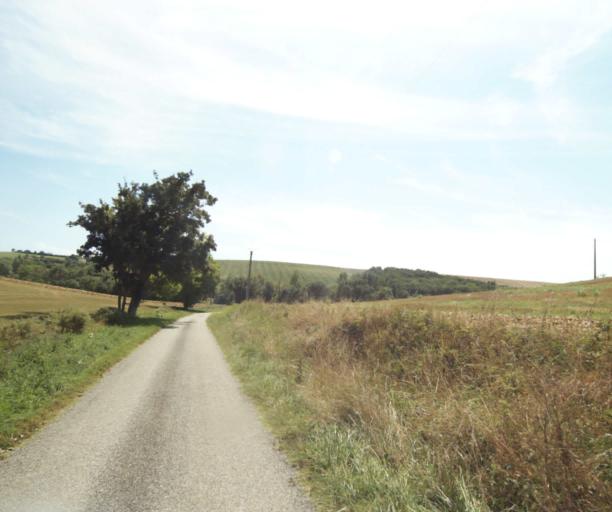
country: FR
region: Midi-Pyrenees
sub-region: Departement de l'Ariege
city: Lezat-sur-Leze
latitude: 43.2602
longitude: 1.4046
